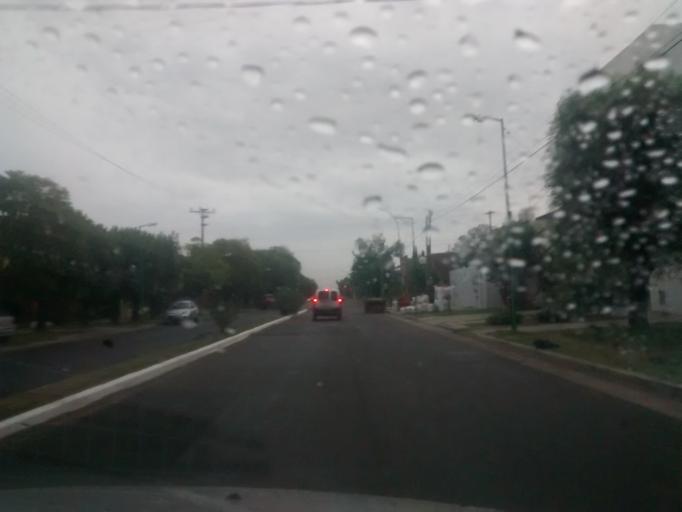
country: AR
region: Buenos Aires
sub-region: Partido de La Plata
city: La Plata
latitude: -34.9066
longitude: -58.0156
